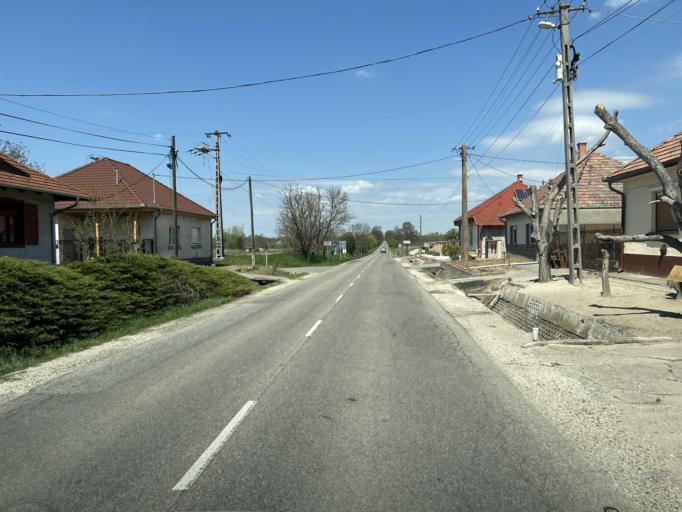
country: HU
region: Pest
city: Ujhartyan
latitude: 47.2241
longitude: 19.3810
